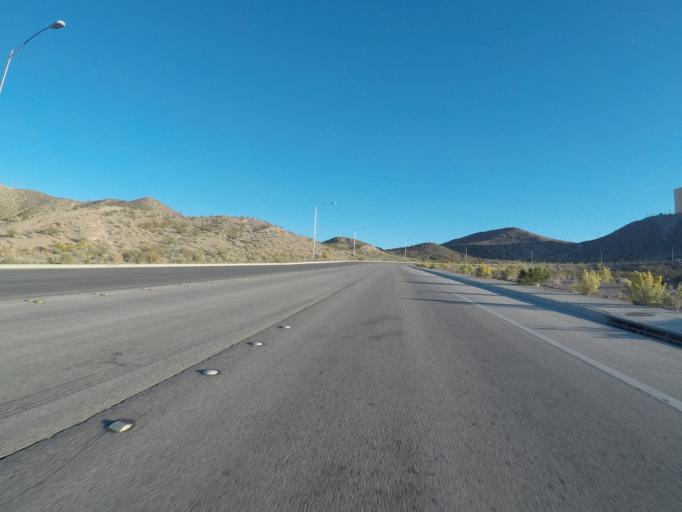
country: US
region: Nevada
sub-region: Clark County
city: Boulder City
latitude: 35.9846
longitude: -114.8287
